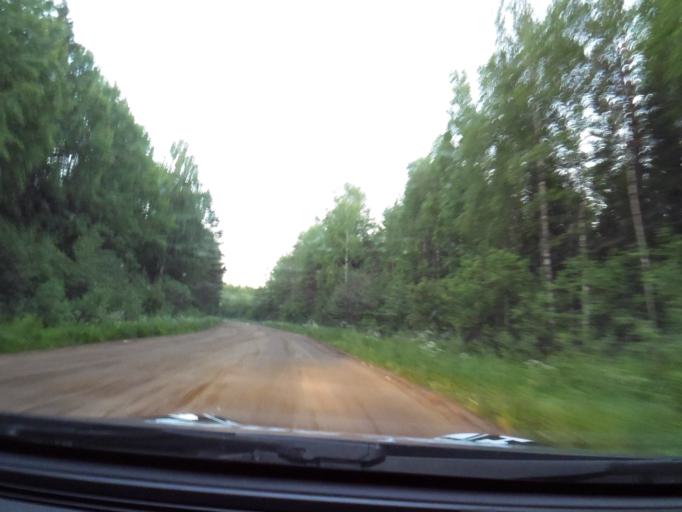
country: RU
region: Leningrad
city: Voznesen'ye
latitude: 60.8538
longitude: 35.8873
